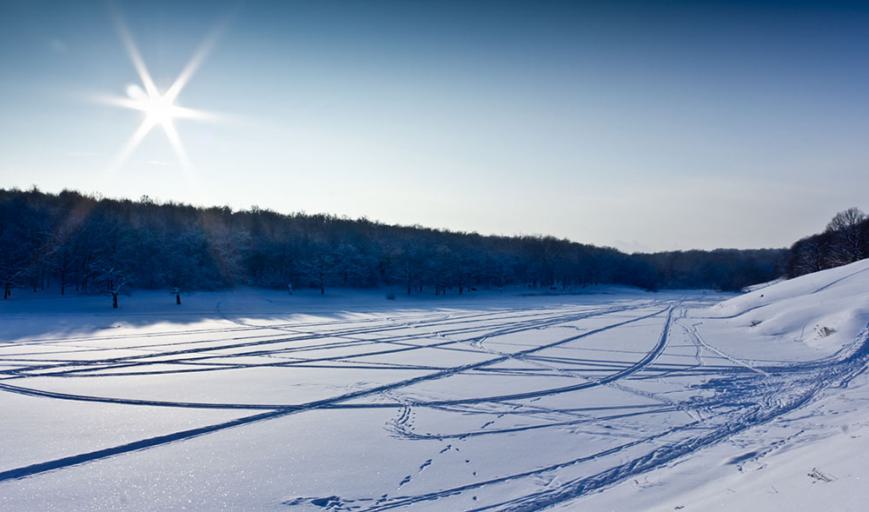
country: RU
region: Nizjnij Novgorod
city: Nizhniy Novgorod
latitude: 56.2767
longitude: 44.0239
